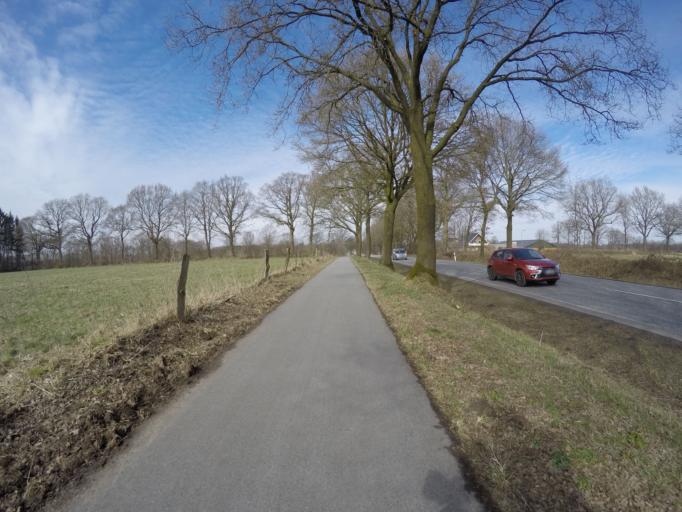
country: DE
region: Schleswig-Holstein
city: Langeln
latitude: 53.7996
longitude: 9.8776
